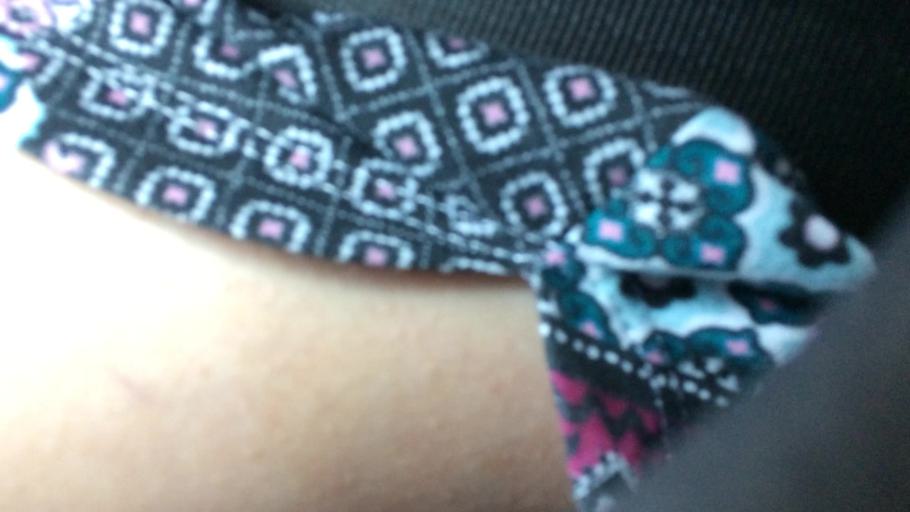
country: US
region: New Mexico
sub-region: Colfax County
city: Springer
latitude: 36.1942
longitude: -104.6666
